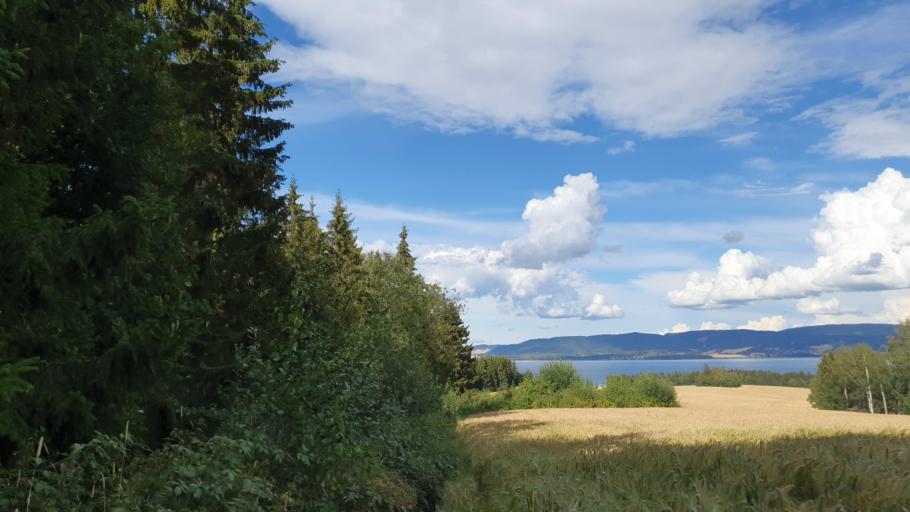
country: NO
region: Nord-Trondelag
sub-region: Levanger
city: Levanger
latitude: 63.7731
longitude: 11.3784
